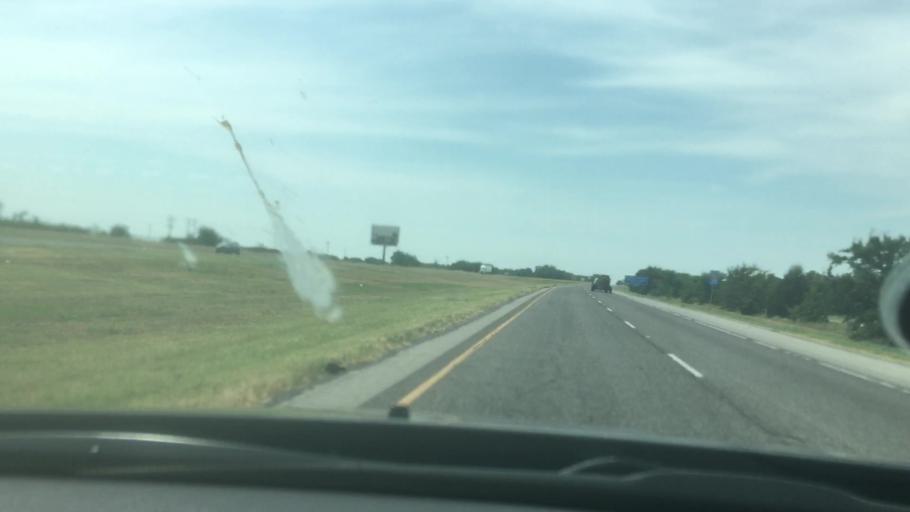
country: US
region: Oklahoma
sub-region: Garvin County
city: Wynnewood
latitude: 34.5649
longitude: -97.1960
